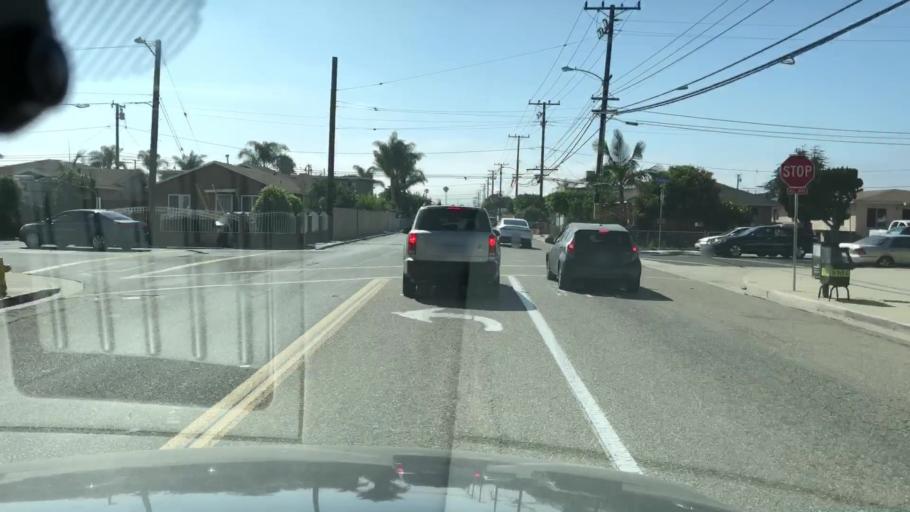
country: US
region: California
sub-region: Ventura County
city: Oxnard
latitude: 34.2064
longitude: -119.1682
